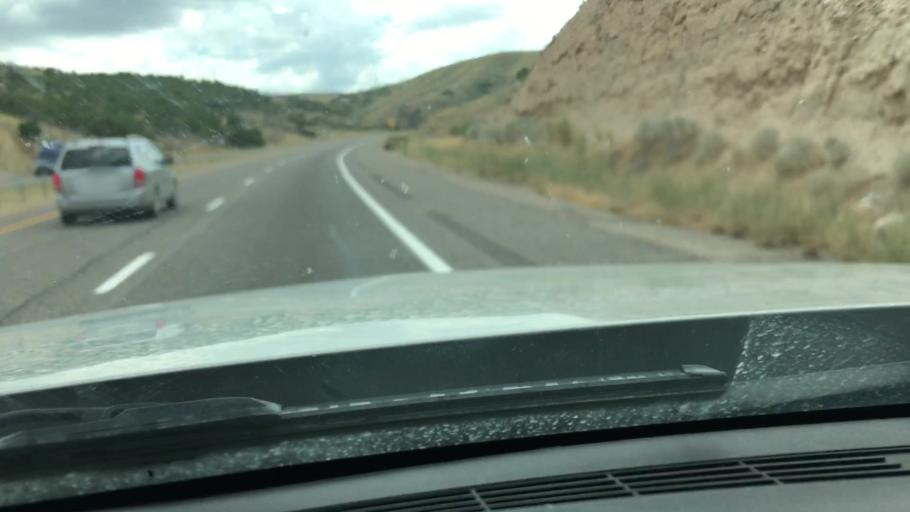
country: US
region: Utah
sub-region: Millard County
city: Fillmore
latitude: 38.6963
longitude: -112.6021
